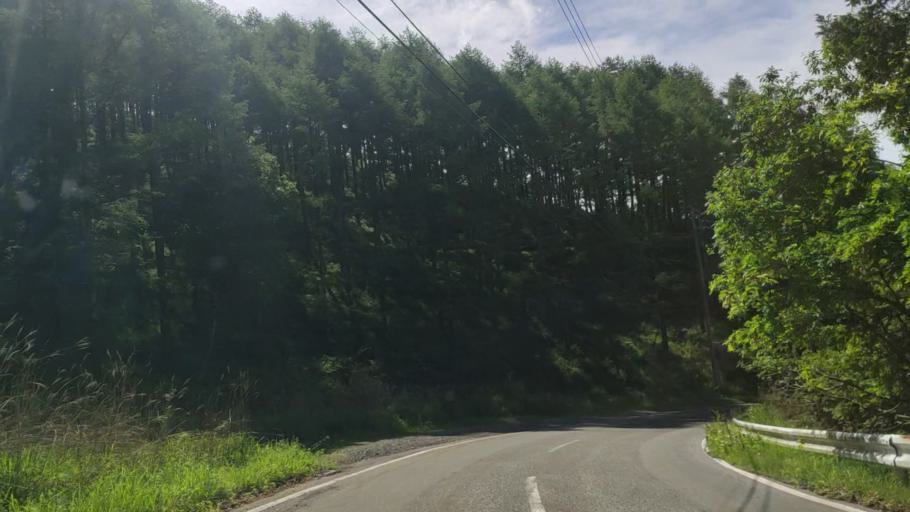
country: JP
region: Nagano
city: Suwa
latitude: 36.0927
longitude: 138.1451
